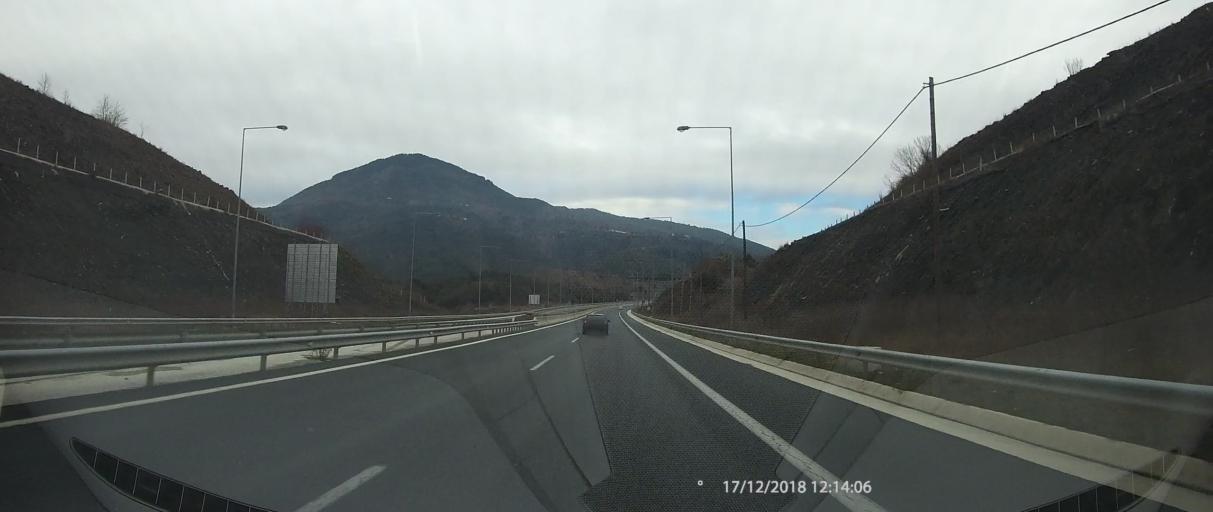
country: GR
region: Epirus
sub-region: Nomos Ioanninon
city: Katsikas
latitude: 39.7150
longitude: 20.9885
